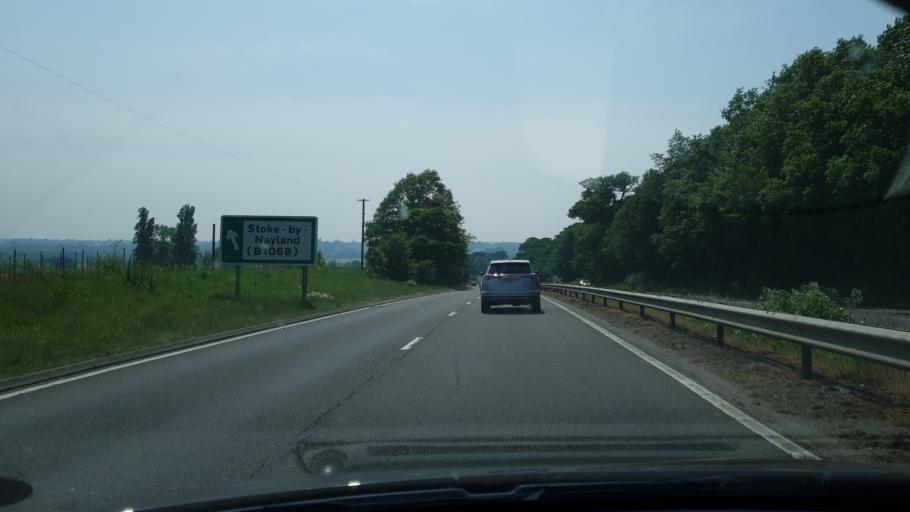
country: GB
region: England
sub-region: Suffolk
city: East Bergholt
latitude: 51.9777
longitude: 0.9903
